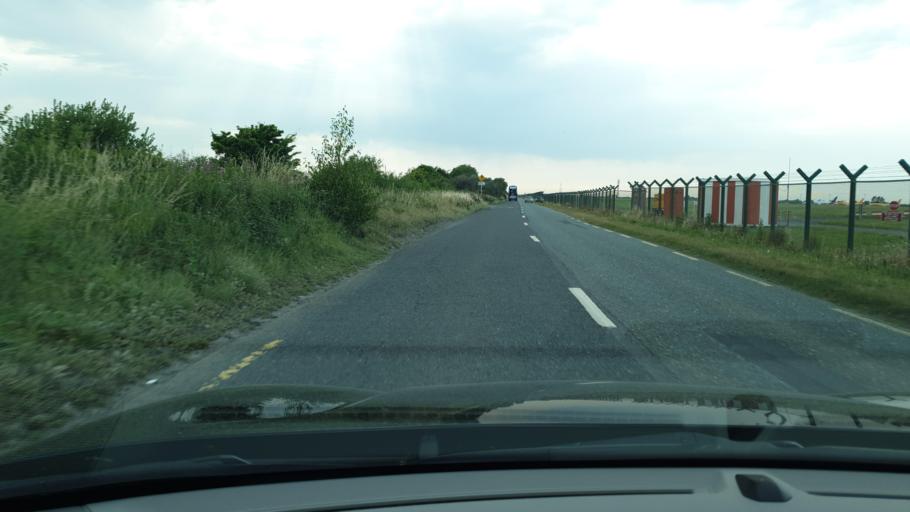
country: IE
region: Leinster
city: Beaumont
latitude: 53.4176
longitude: -6.2478
